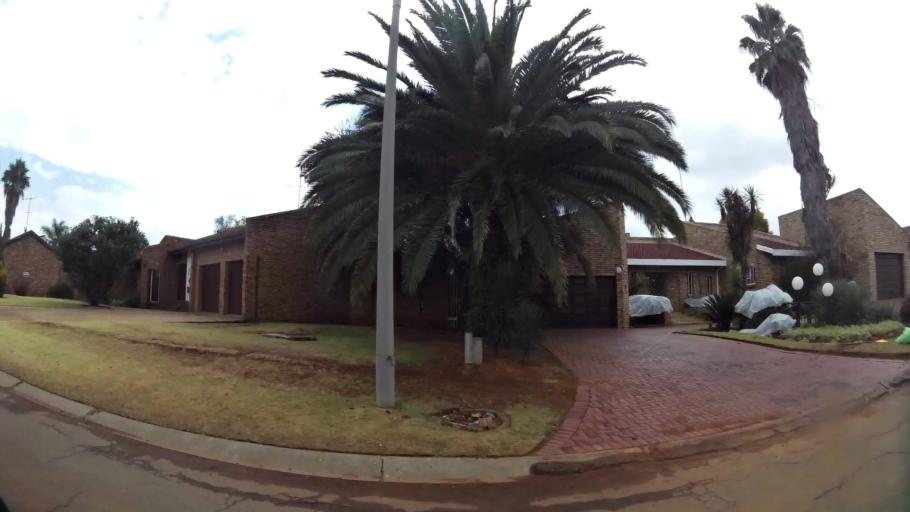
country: ZA
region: Gauteng
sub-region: Sedibeng District Municipality
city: Vanderbijlpark
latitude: -26.7403
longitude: 27.8504
